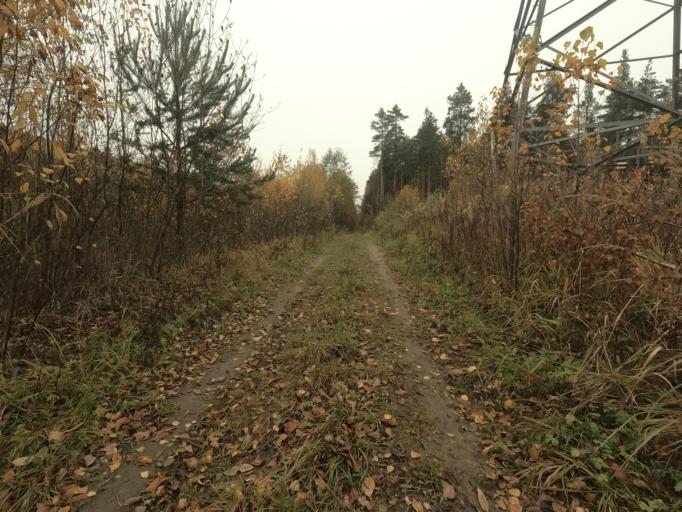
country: RU
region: Leningrad
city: Pavlovo
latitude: 59.7744
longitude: 30.9035
